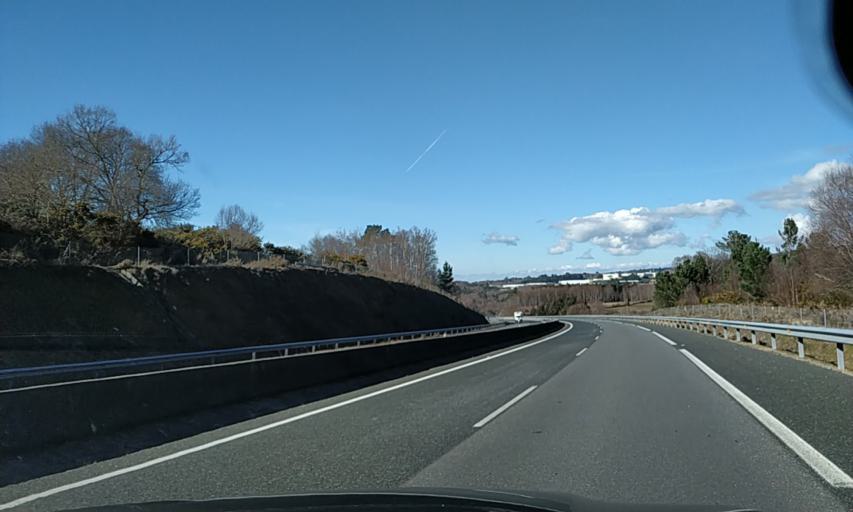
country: ES
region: Galicia
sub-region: Provincia de Pontevedra
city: Lalin
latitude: 42.6579
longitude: -8.1406
